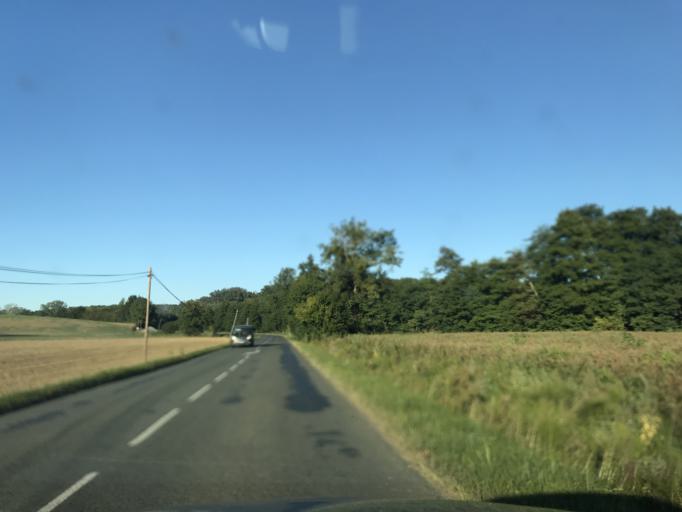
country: FR
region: Aquitaine
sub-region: Departement de la Gironde
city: Rauzan
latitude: 44.7551
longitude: -0.0711
